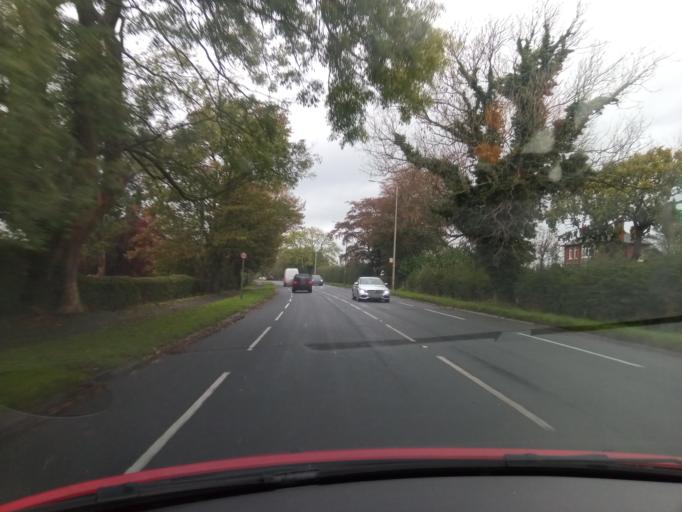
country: GB
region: England
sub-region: Lancashire
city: Catterall
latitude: 53.8463
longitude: -2.7439
